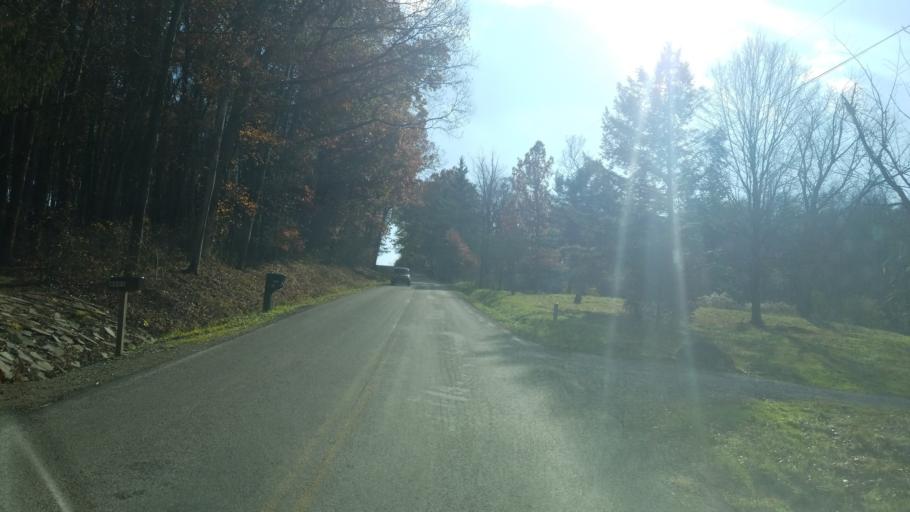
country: US
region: Ohio
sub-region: Sandusky County
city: Bellville
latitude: 40.6270
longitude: -82.4441
